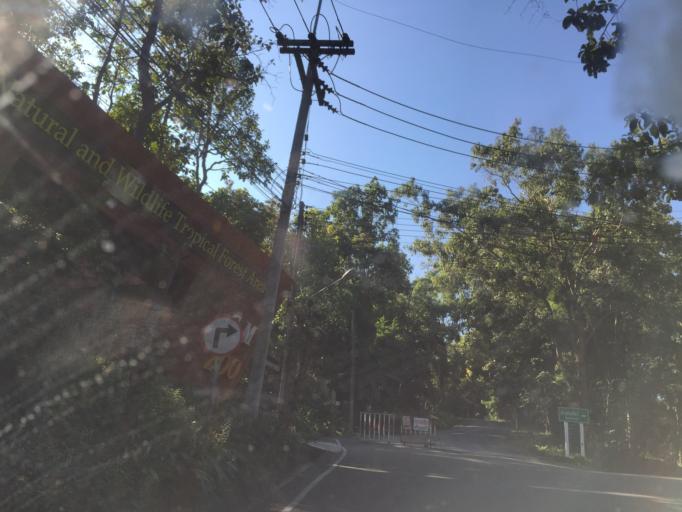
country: TH
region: Chiang Mai
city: Chiang Mai
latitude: 18.8023
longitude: 98.9442
